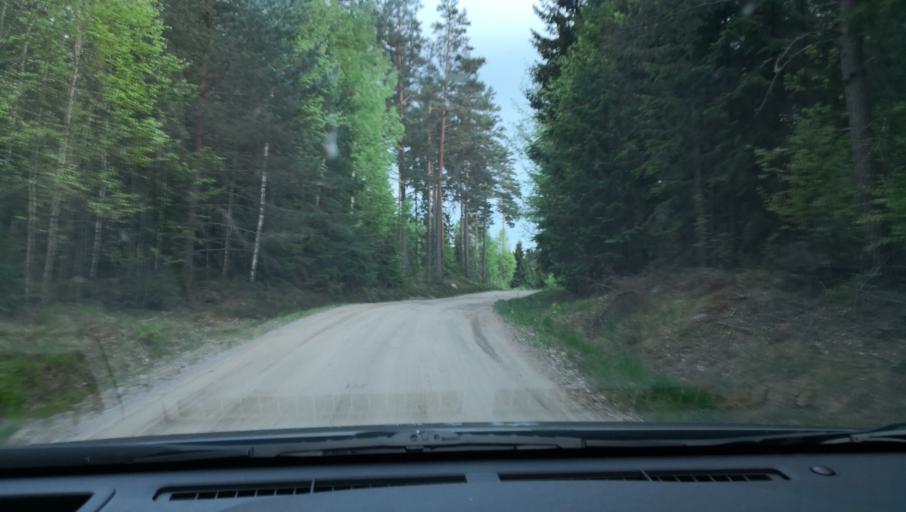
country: SE
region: Vaestmanland
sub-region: Skinnskattebergs Kommun
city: Skinnskatteberg
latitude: 59.7341
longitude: 15.4724
